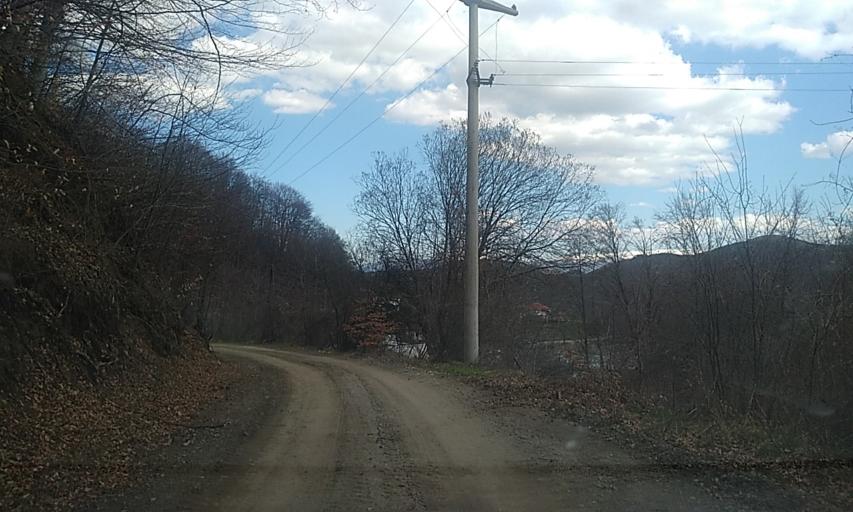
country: RS
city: Radovnica
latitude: 42.3474
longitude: 22.3418
